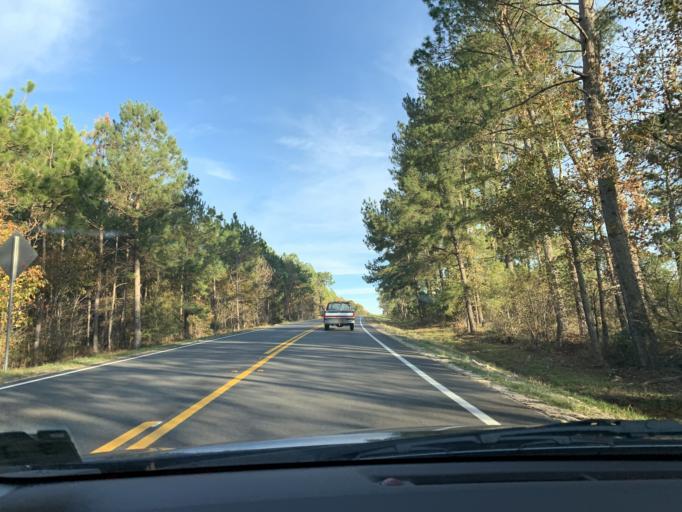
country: US
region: Georgia
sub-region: Irwin County
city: Ocilla
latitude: 31.5947
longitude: -83.1118
